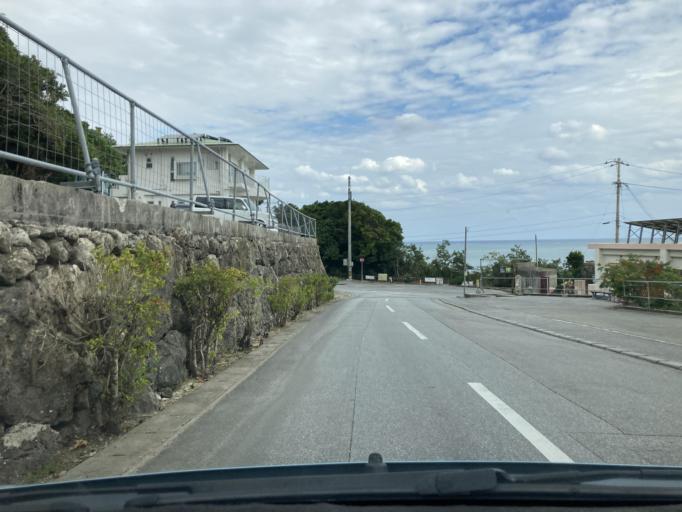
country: JP
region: Okinawa
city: Tomigusuku
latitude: 26.1351
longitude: 127.7906
